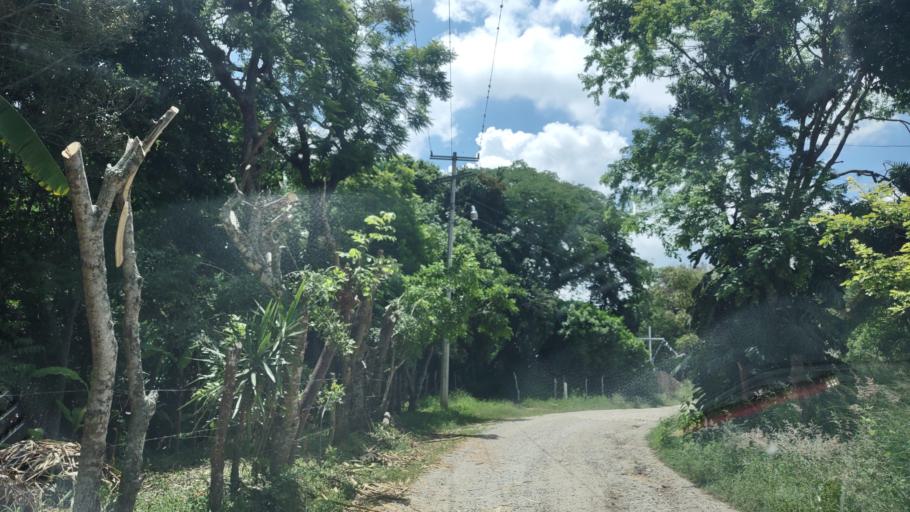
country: MX
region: Veracruz
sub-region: Emiliano Zapata
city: Dos Rios
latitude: 19.4975
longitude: -96.8123
